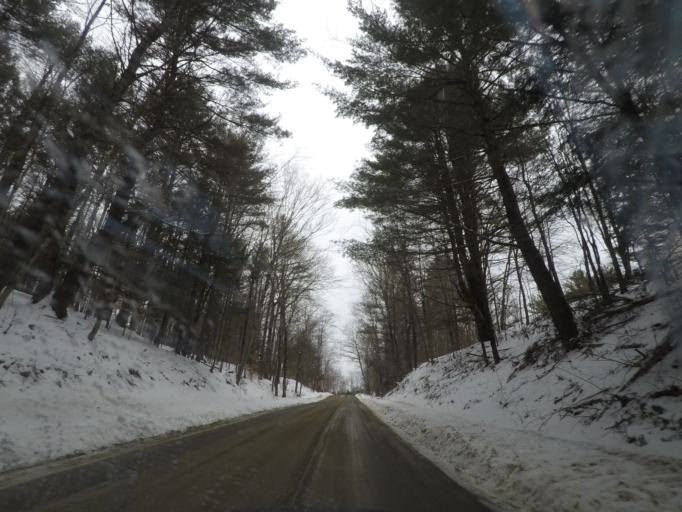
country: US
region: Massachusetts
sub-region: Berkshire County
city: Richmond
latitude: 42.5392
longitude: -73.4078
